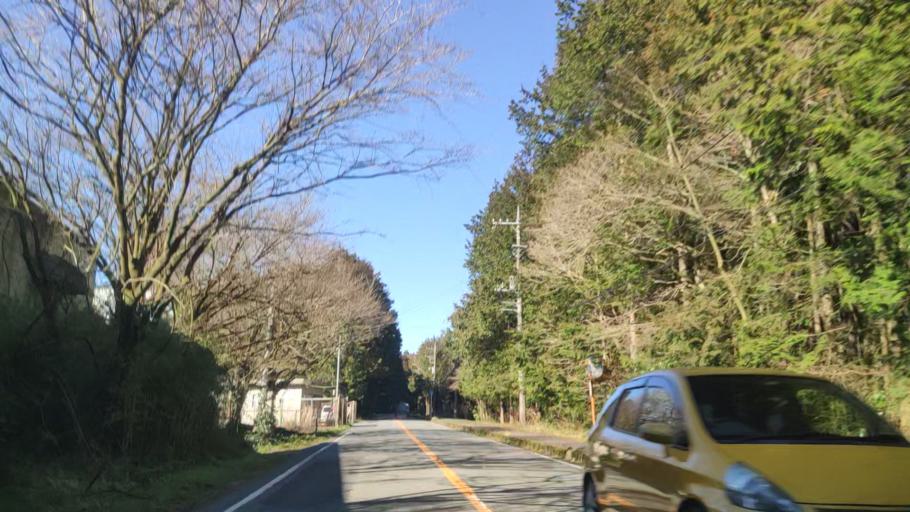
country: JP
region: Shizuoka
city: Fujinomiya
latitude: 35.3224
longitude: 138.5916
